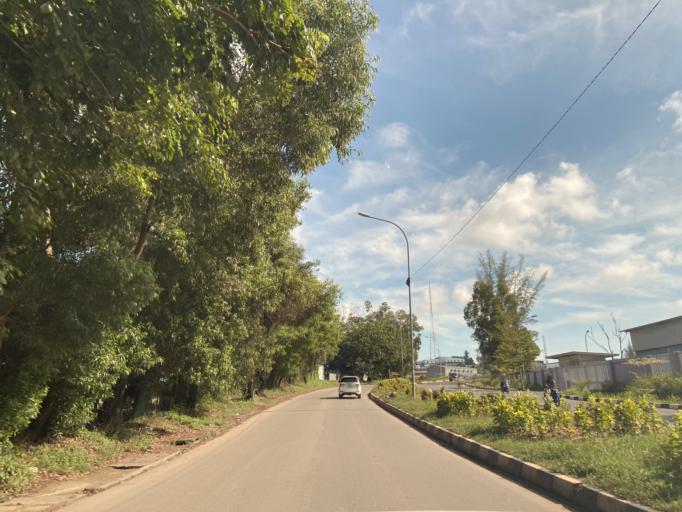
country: SG
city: Singapore
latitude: 1.1700
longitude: 104.0117
